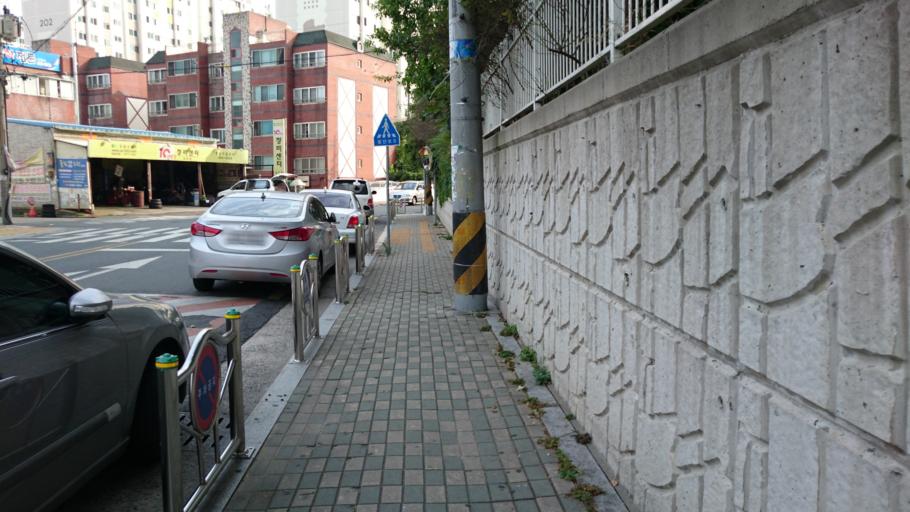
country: KR
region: Daegu
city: Daegu
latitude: 35.8807
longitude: 128.6614
